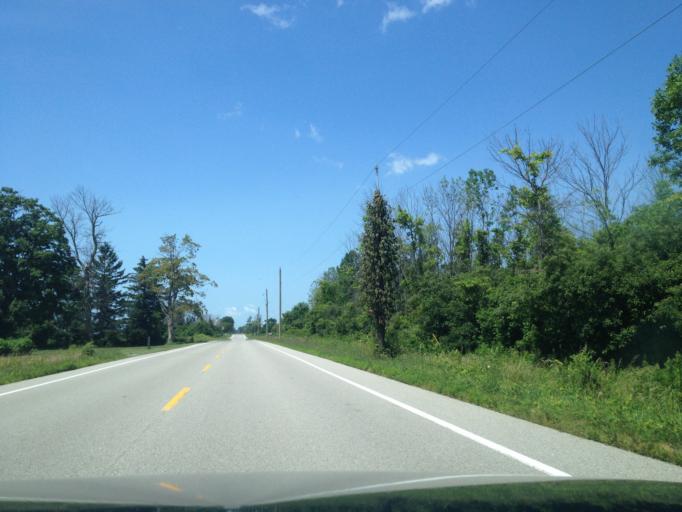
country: CA
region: Ontario
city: Norfolk County
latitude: 42.5781
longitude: -80.5589
